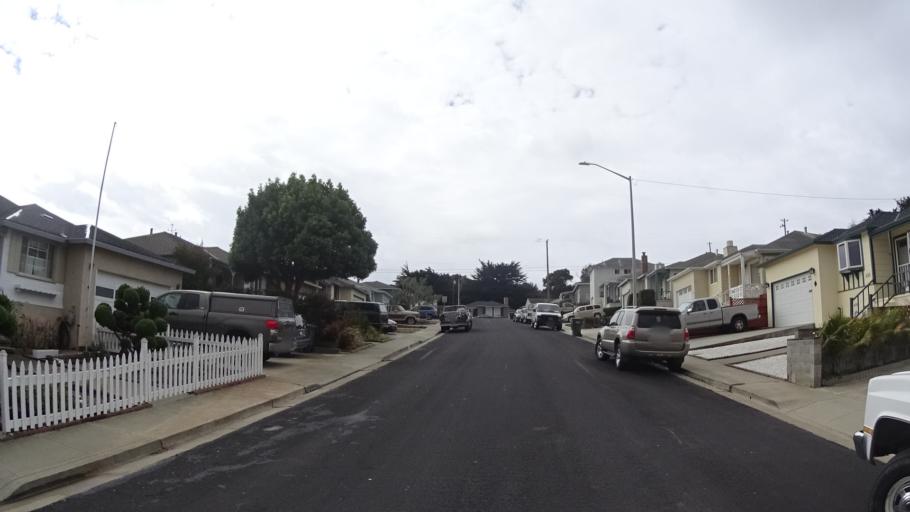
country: US
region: California
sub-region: San Mateo County
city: San Bruno
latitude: 37.6376
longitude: -122.4344
